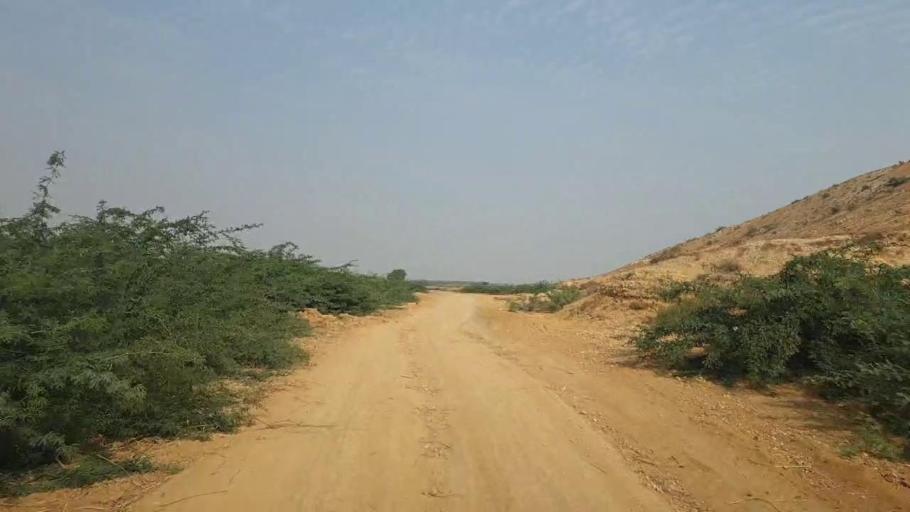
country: PK
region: Sindh
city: Tando Muhammad Khan
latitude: 25.1382
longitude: 68.4565
